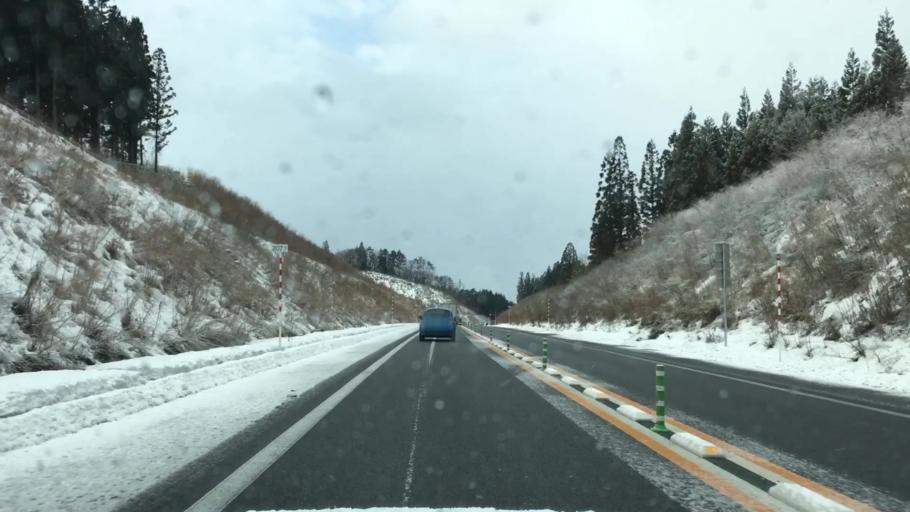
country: JP
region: Akita
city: Takanosu
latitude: 40.2126
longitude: 140.4180
